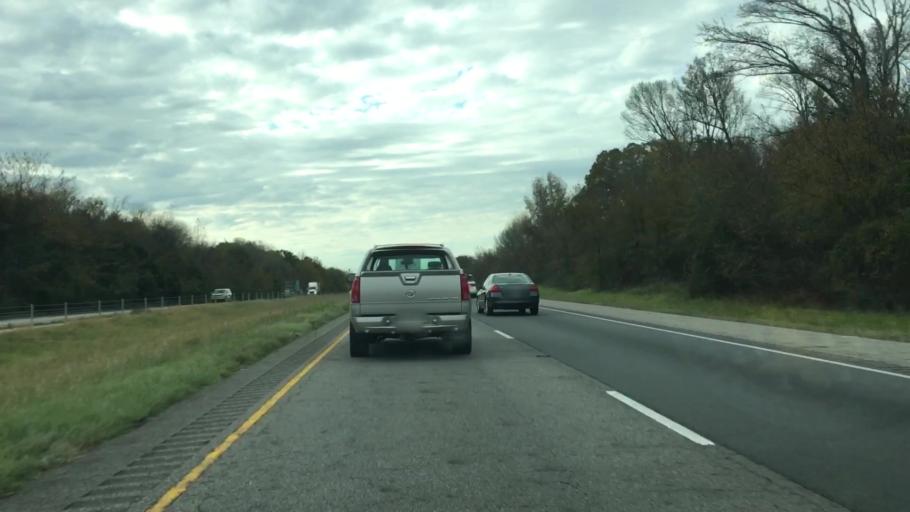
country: US
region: Arkansas
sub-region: Conway County
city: Morrilton
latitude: 35.1624
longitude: -92.6116
